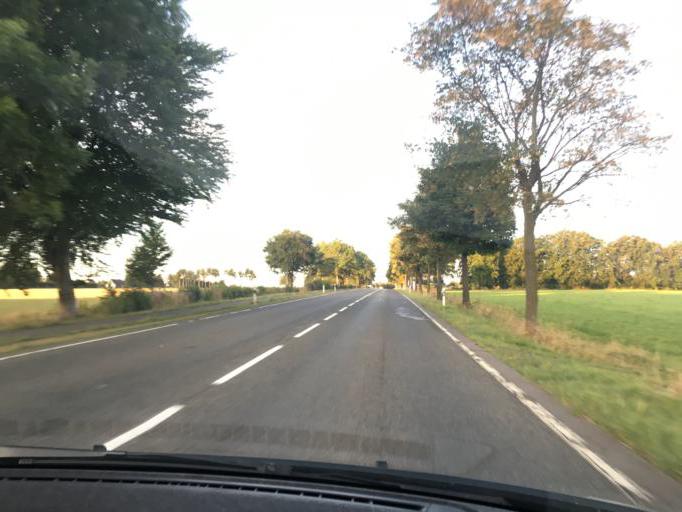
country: DE
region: North Rhine-Westphalia
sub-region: Regierungsbezirk Koln
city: Simmerath
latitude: 50.5962
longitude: 6.2899
